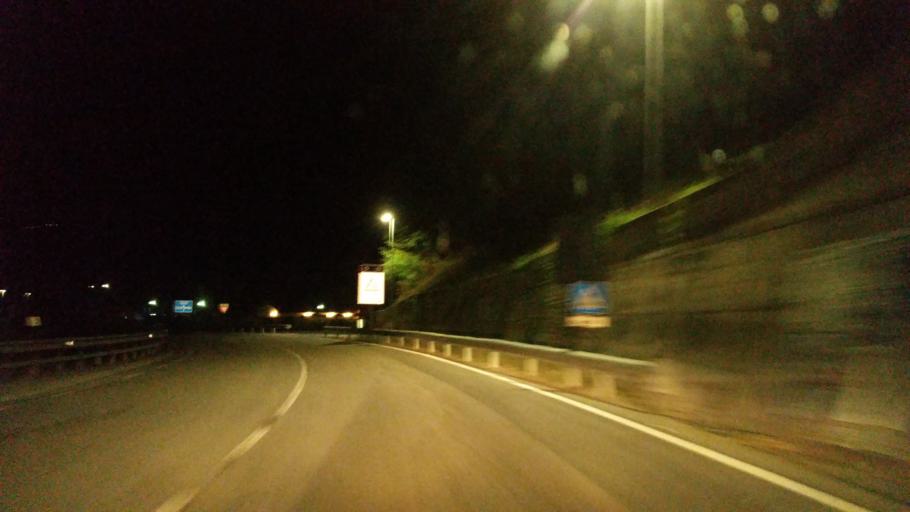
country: IT
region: Piedmont
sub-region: Provincia di Cuneo
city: Camerana
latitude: 44.4414
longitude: 8.1488
